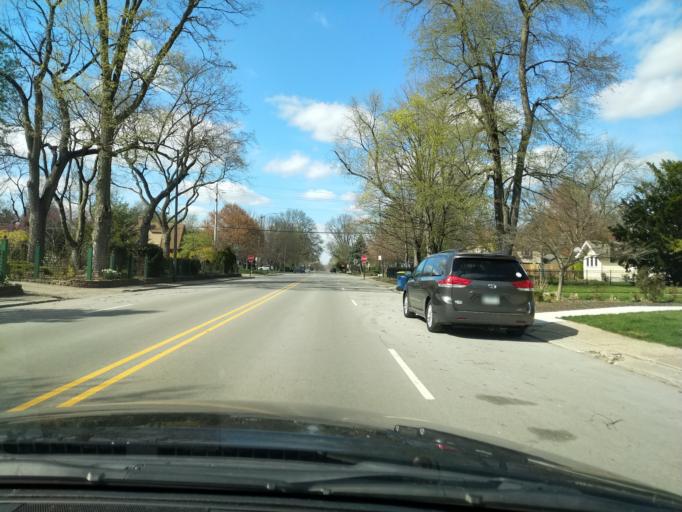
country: US
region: Indiana
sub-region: Marion County
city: Broad Ripple
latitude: 39.8591
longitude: -86.1502
